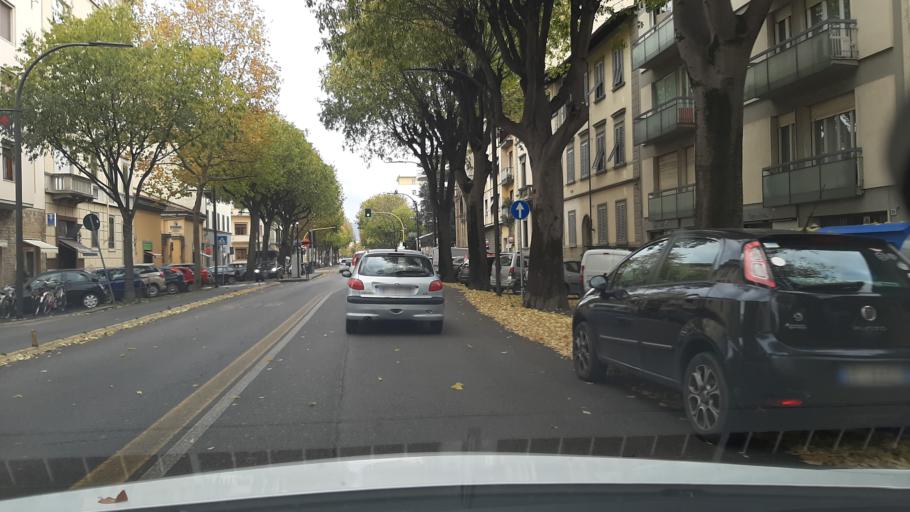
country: IT
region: Tuscany
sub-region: Province of Florence
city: Fiesole
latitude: 43.7815
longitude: 11.2777
